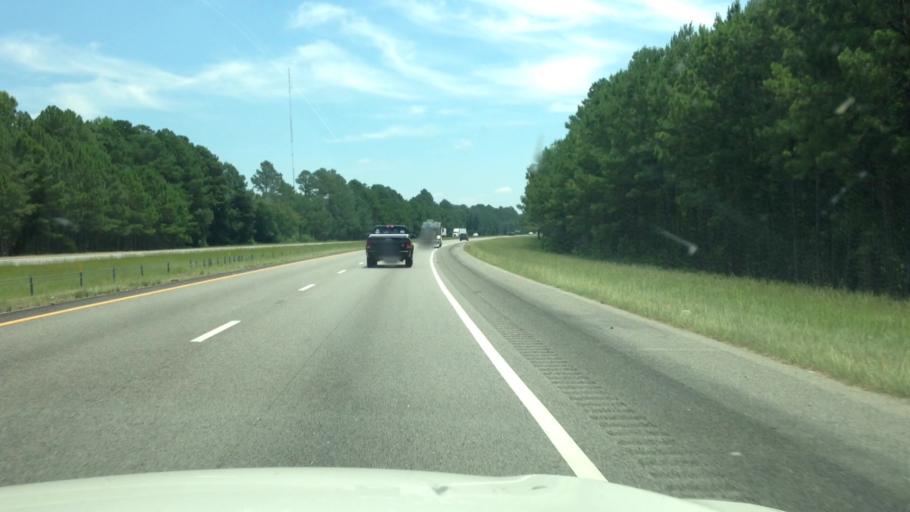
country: US
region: South Carolina
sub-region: Darlington County
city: Darlington
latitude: 34.2042
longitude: -79.8733
